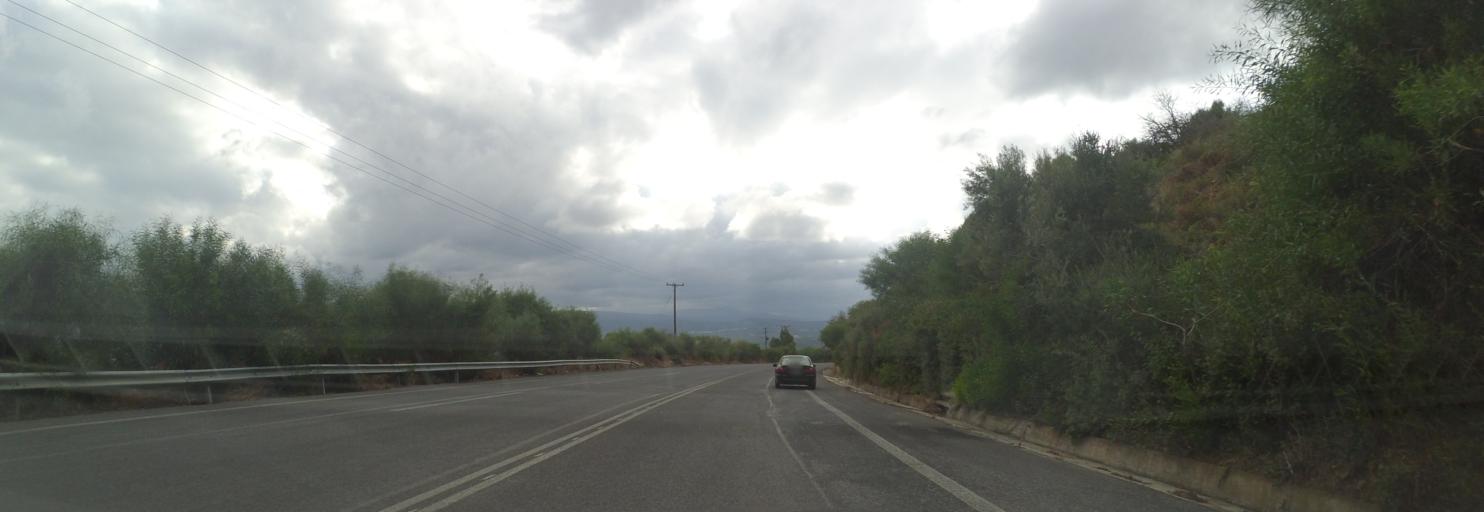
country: GR
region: Crete
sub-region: Nomos Rethymnis
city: Panormos
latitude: 35.4083
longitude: 24.7441
